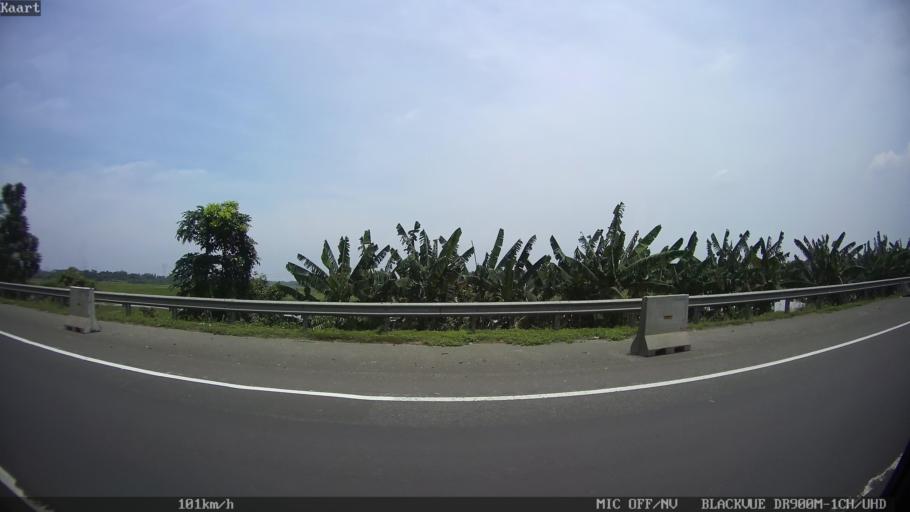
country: ID
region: West Java
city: Kresek
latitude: -6.1836
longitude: 106.3989
